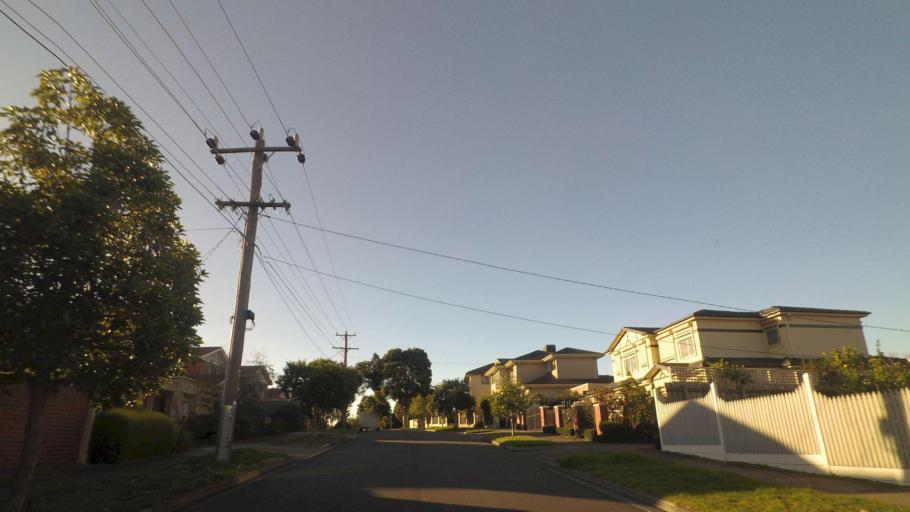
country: AU
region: Victoria
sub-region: Manningham
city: Doncaster East
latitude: -37.7928
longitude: 145.1566
